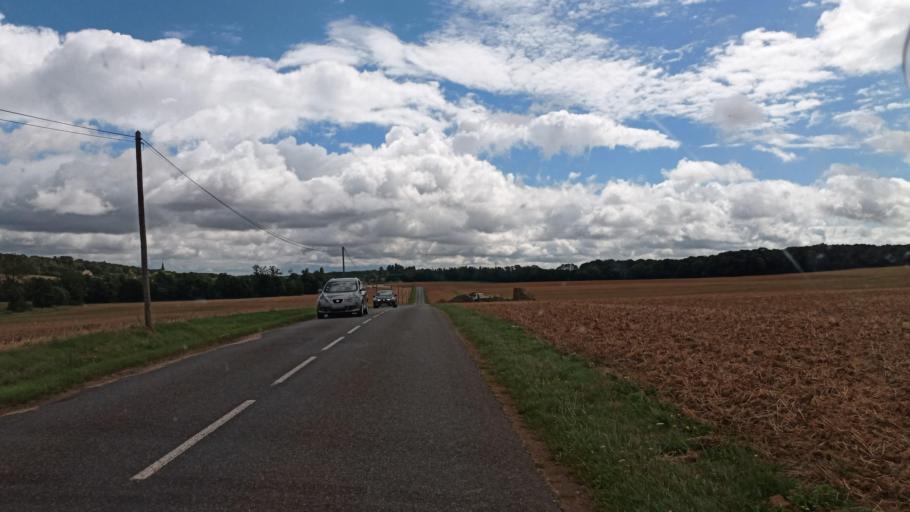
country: FR
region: Bourgogne
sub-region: Departement de l'Yonne
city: Cheroy
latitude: 48.2483
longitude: 3.0327
